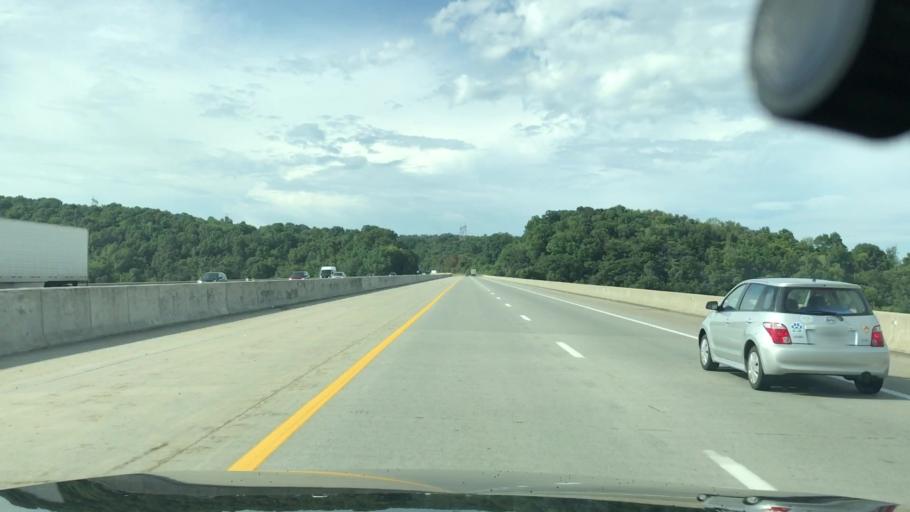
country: US
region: Virginia
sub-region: Carroll County
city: Woodlawn
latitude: 36.8705
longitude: -80.8721
